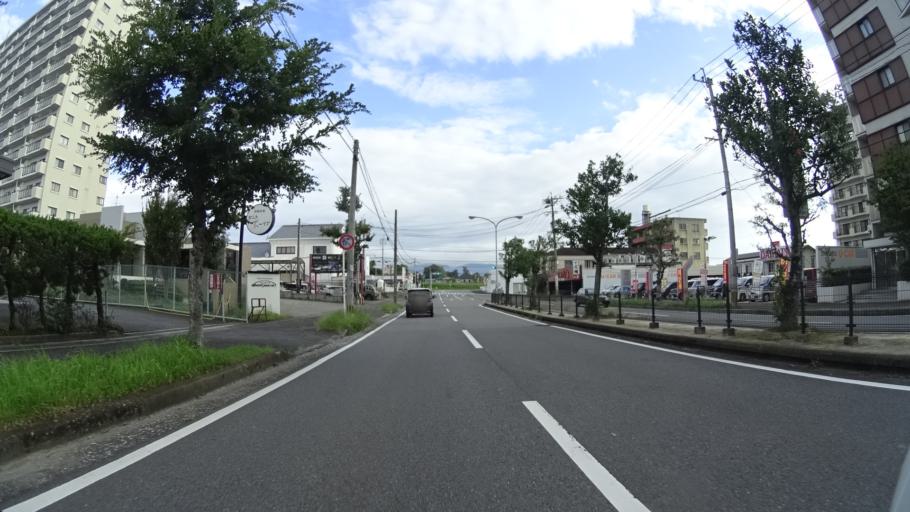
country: JP
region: Oita
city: Beppu
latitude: 33.3044
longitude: 131.4947
